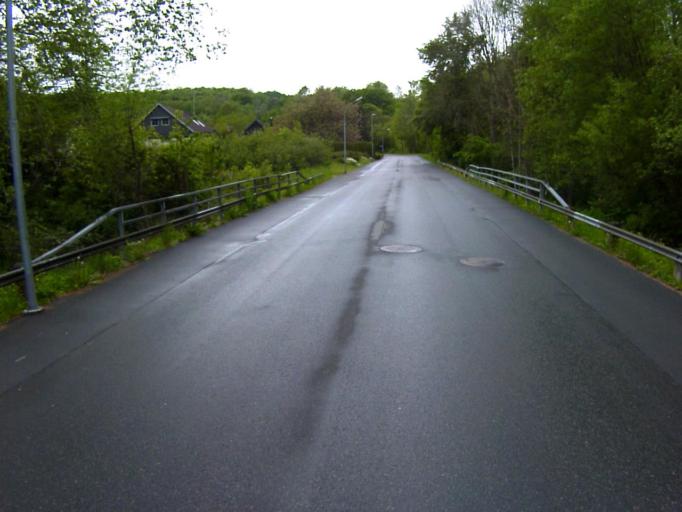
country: SE
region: Skane
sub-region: Kristianstads Kommun
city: Degeberga
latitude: 55.8290
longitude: 14.0835
